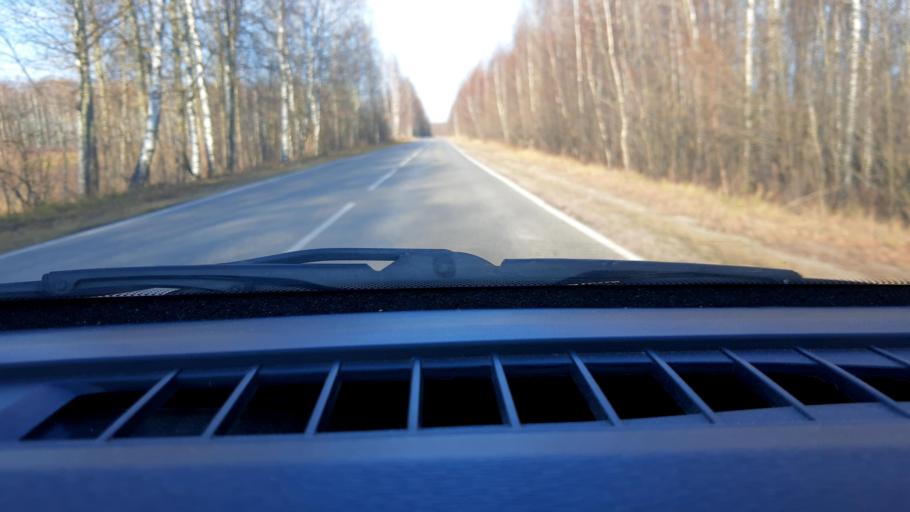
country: RU
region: Nizjnij Novgorod
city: Neklyudovo
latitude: 56.5065
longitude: 43.8432
